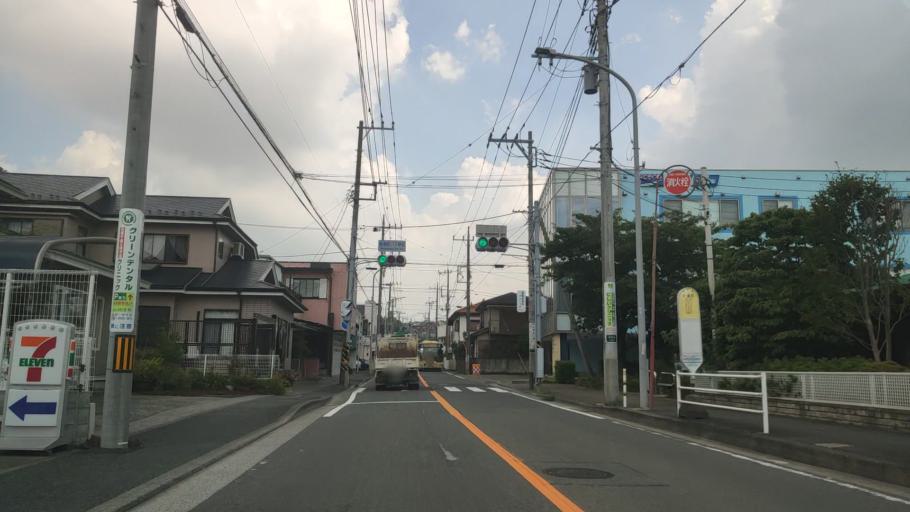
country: JP
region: Kanagawa
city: Minami-rinkan
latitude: 35.4332
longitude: 139.5129
